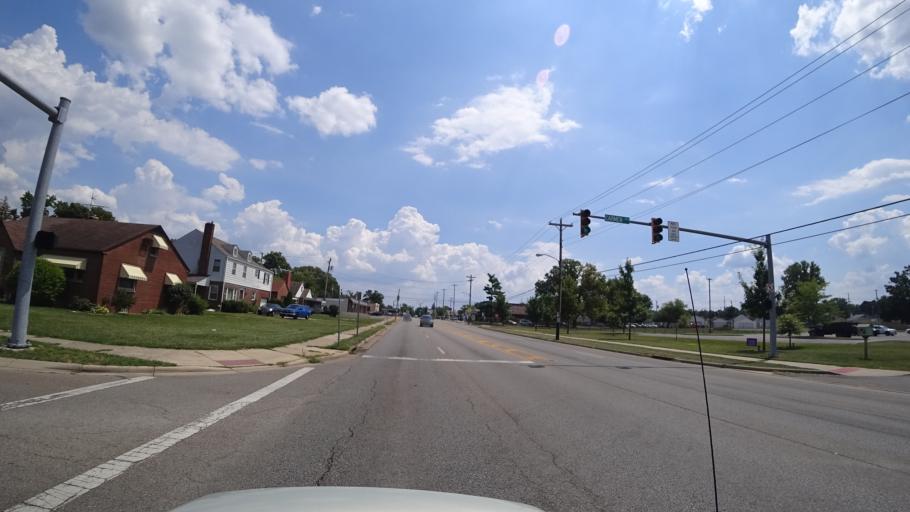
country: US
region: Ohio
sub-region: Butler County
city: Hamilton
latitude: 39.4154
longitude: -84.5839
